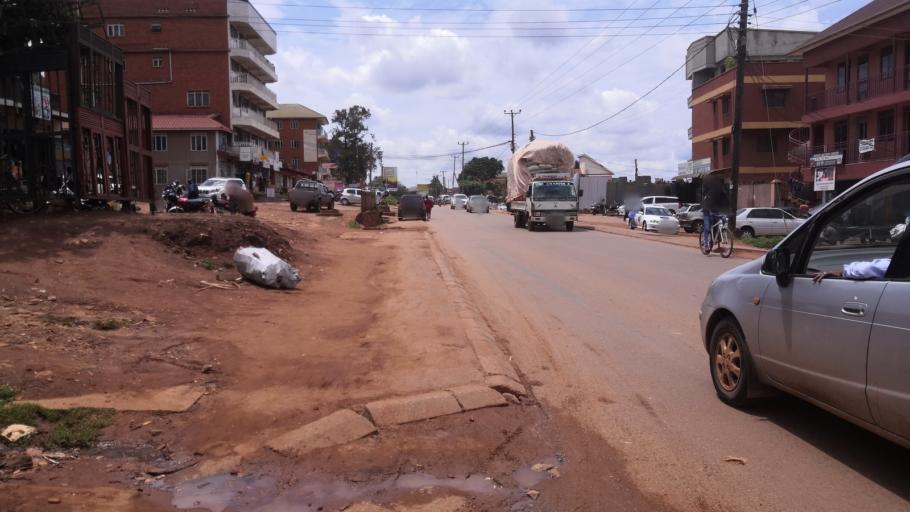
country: UG
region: Central Region
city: Kampala Central Division
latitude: 0.3446
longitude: 32.5691
